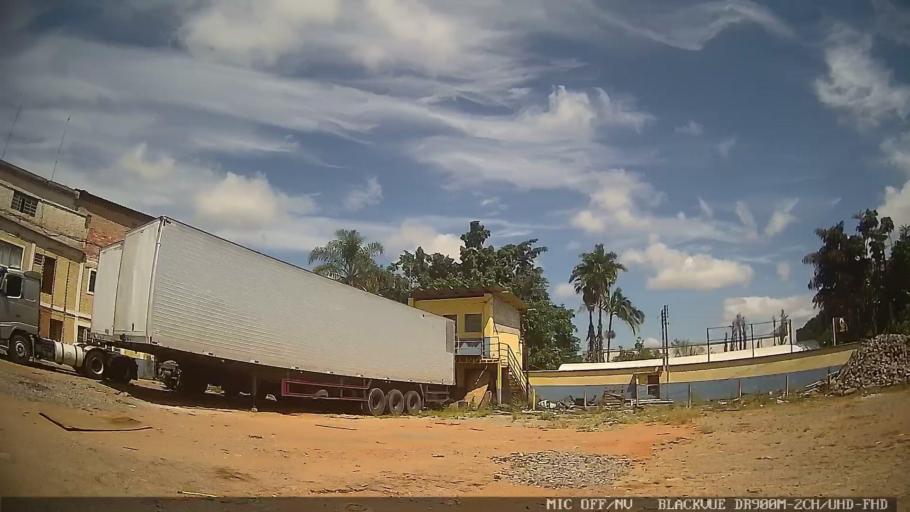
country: BR
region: Sao Paulo
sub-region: Braganca Paulista
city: Braganca Paulista
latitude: -22.9888
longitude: -46.5490
